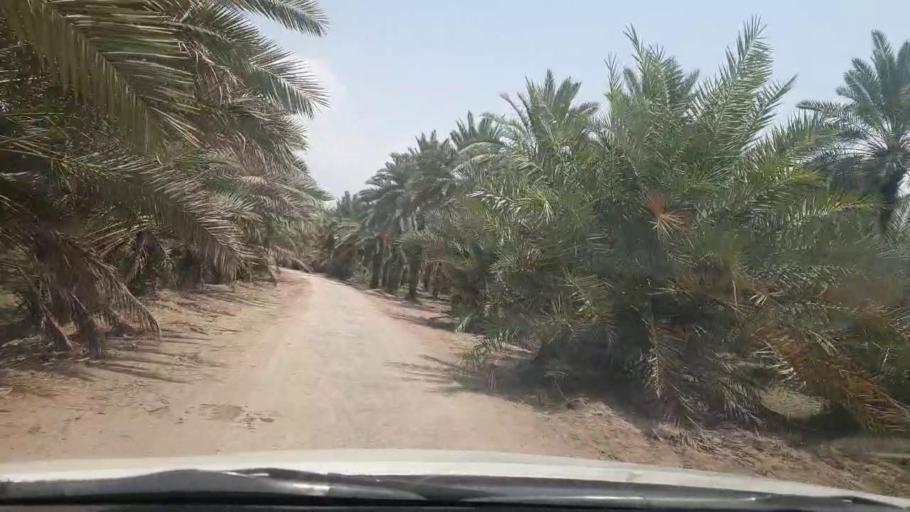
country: PK
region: Sindh
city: Khairpur
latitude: 27.5500
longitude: 68.8339
